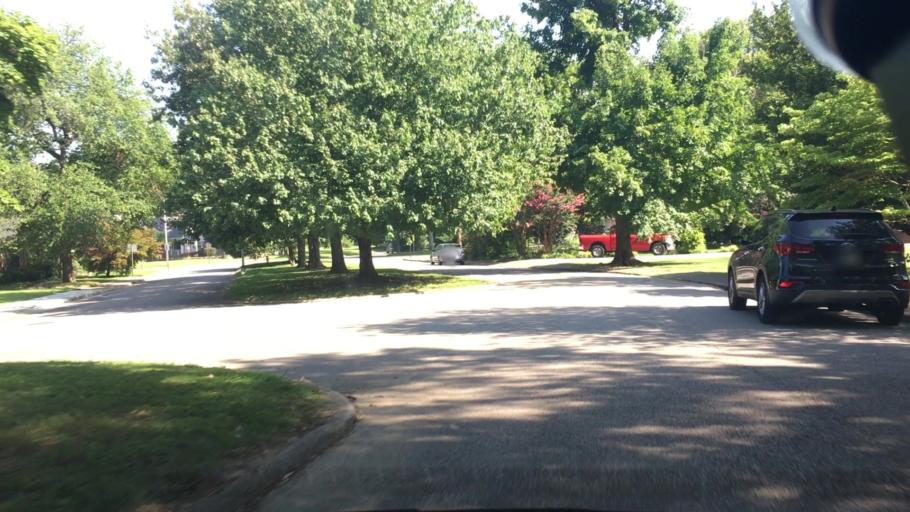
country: US
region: Indiana
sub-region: Vanderburgh County
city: Evansville
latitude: 37.9727
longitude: -87.5244
